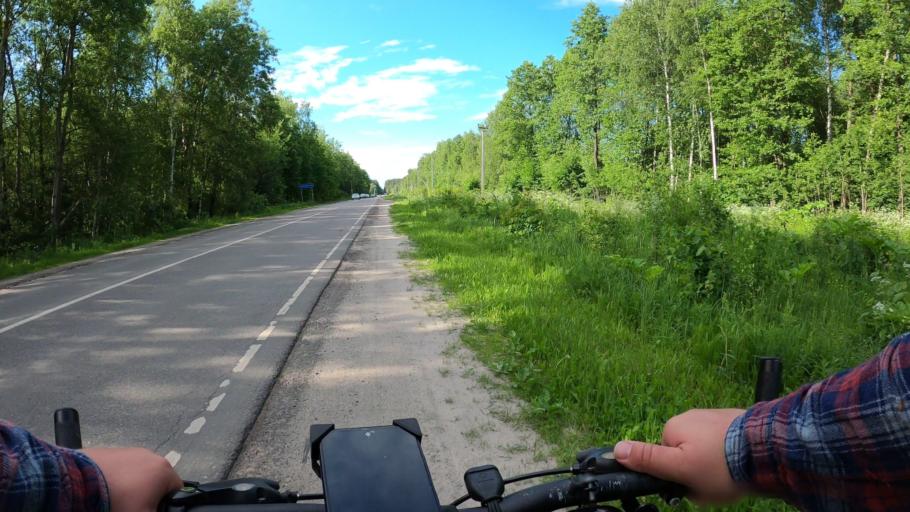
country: RU
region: Moskovskaya
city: Konobeyevo
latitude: 55.4298
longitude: 38.6622
